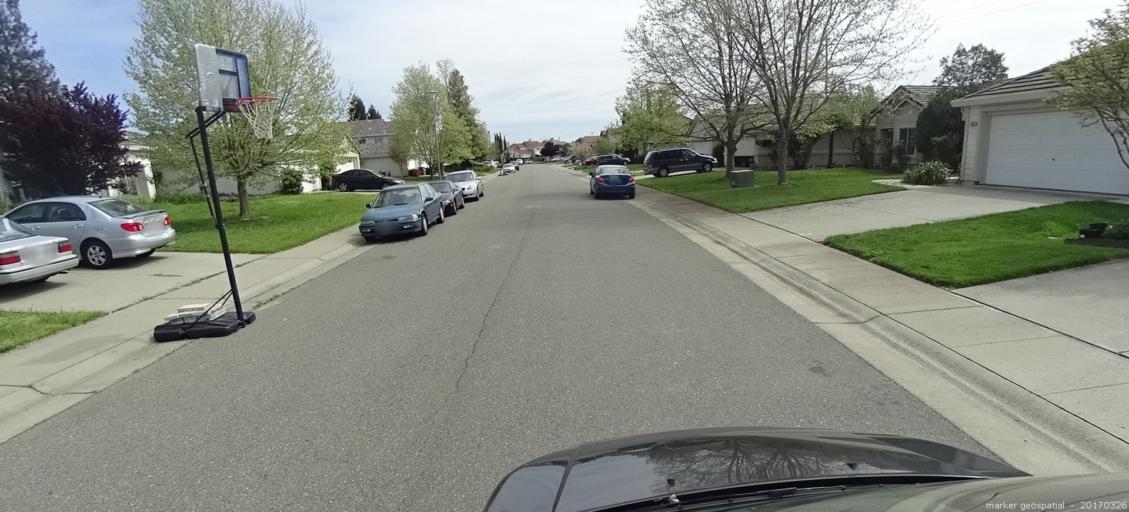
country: US
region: California
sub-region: Sacramento County
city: Laguna
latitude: 38.4383
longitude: -121.4313
